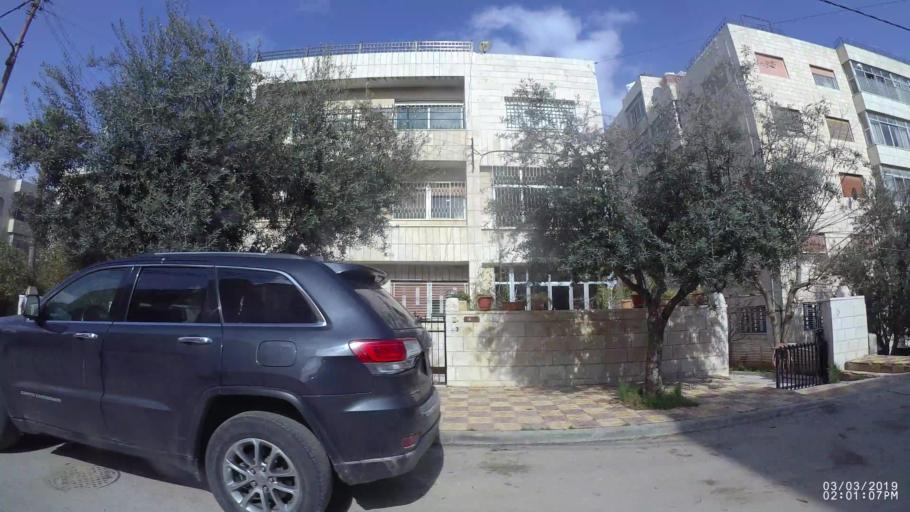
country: JO
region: Amman
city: Al Jubayhah
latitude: 31.9787
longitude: 35.8936
